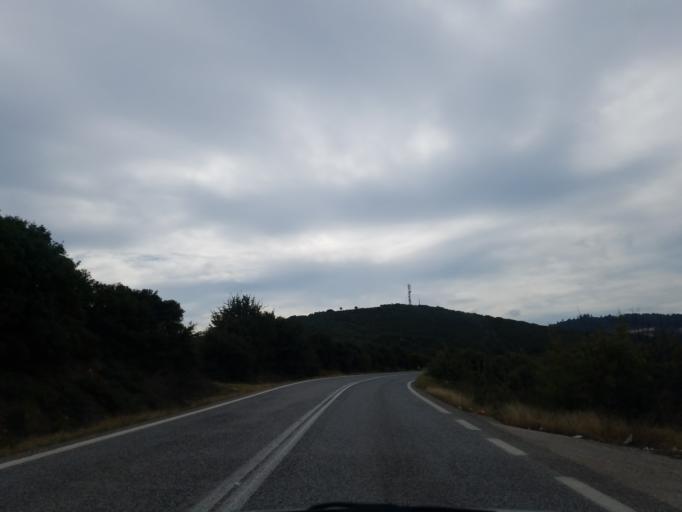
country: GR
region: Central Greece
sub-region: Nomos Fthiotidos
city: Domokos
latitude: 39.1404
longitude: 22.3100
